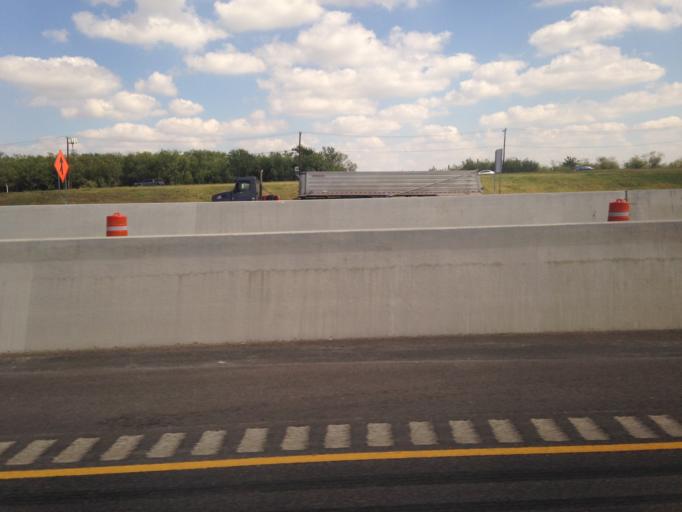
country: US
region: Texas
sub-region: Tarrant County
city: Blue Mound
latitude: 32.8747
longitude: -97.3173
